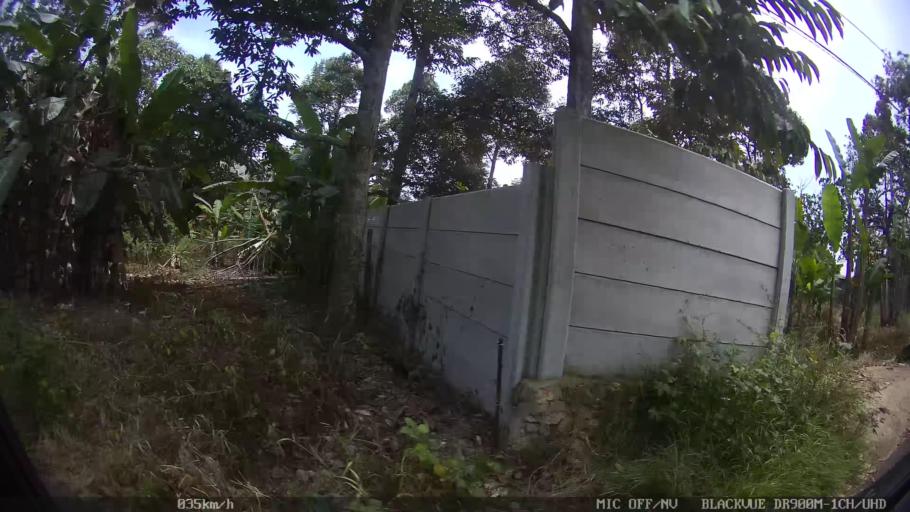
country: ID
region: Lampung
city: Bandarlampung
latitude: -5.4155
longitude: 105.2156
